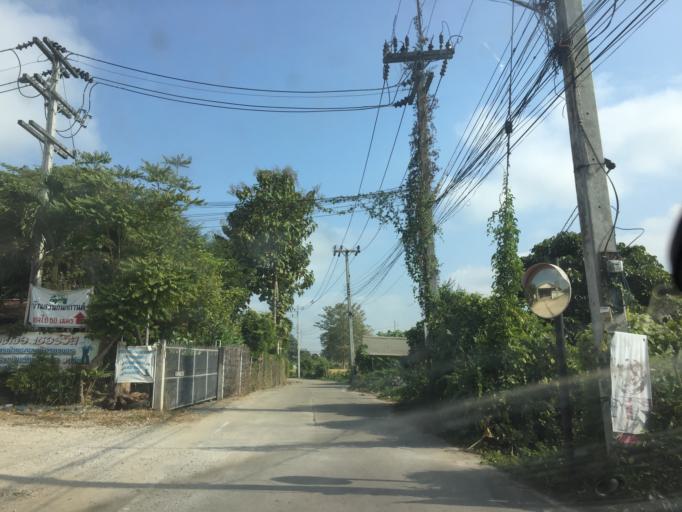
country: TH
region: Lamphun
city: Ban Thi
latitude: 18.6480
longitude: 99.0510
